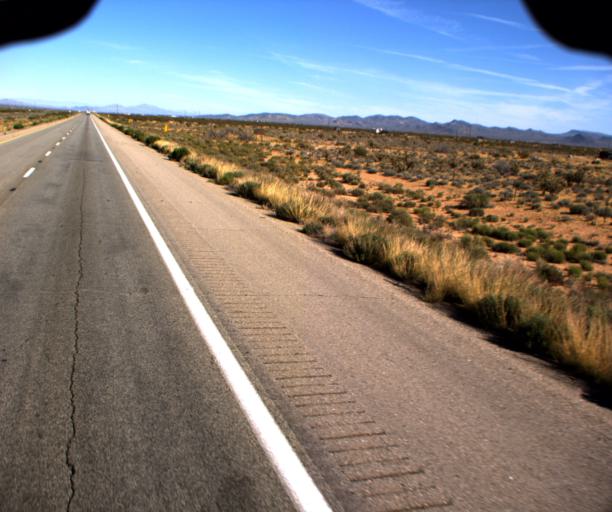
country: US
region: Arizona
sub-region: Mohave County
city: Dolan Springs
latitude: 35.4977
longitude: -114.3301
